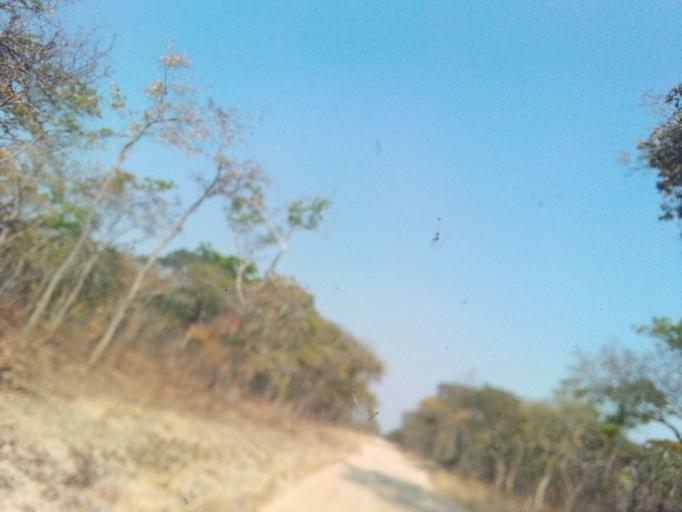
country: ZM
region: Northern
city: Mpika
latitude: -12.2280
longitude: 30.9102
